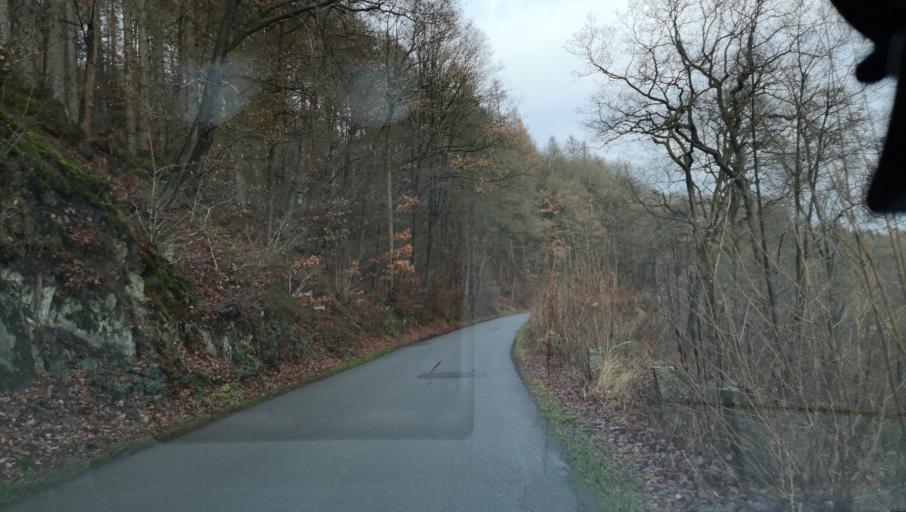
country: DE
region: North Rhine-Westphalia
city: Radevormwald
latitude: 51.2017
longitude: 7.2990
